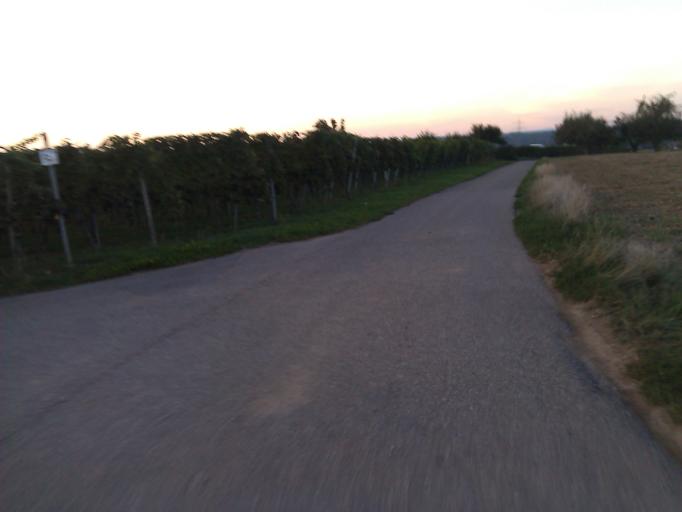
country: DE
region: Baden-Wuerttemberg
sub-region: Regierungsbezirk Stuttgart
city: Talheim
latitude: 49.0959
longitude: 9.1677
